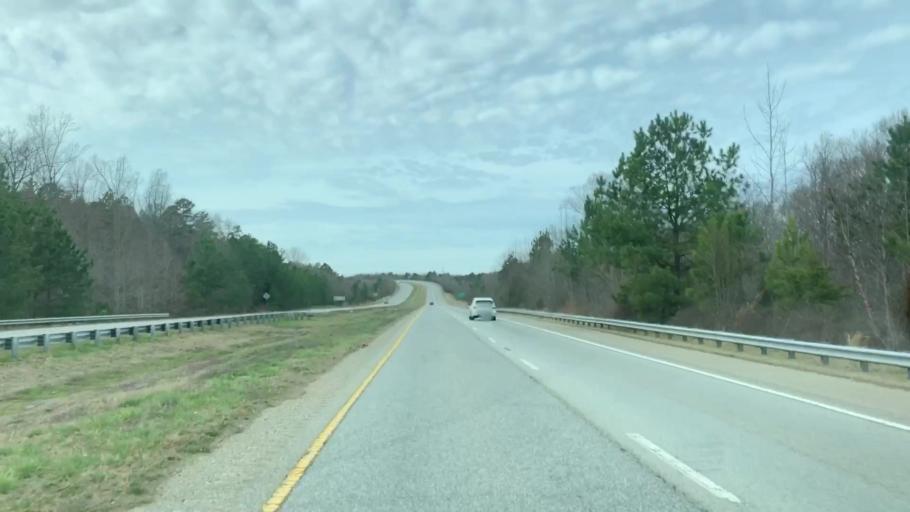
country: US
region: South Carolina
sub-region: Greenville County
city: Golden Grove
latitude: 34.7206
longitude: -82.3679
